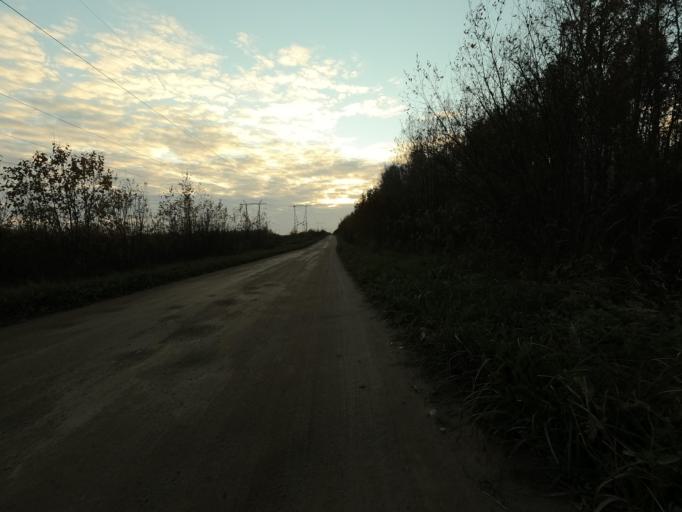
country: RU
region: Leningrad
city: Mga
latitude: 59.8064
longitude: 31.1994
